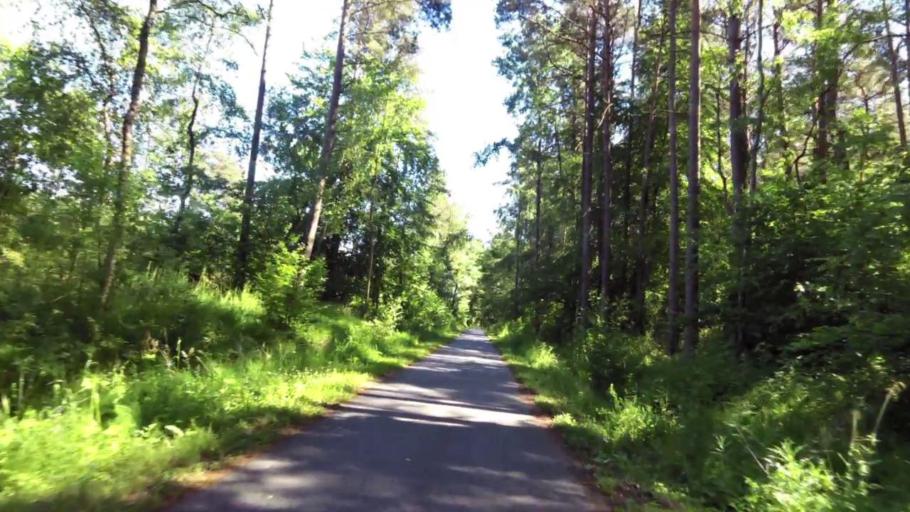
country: PL
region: West Pomeranian Voivodeship
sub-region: Powiat bialogardzki
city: Karlino
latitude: 54.0557
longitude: 15.8742
